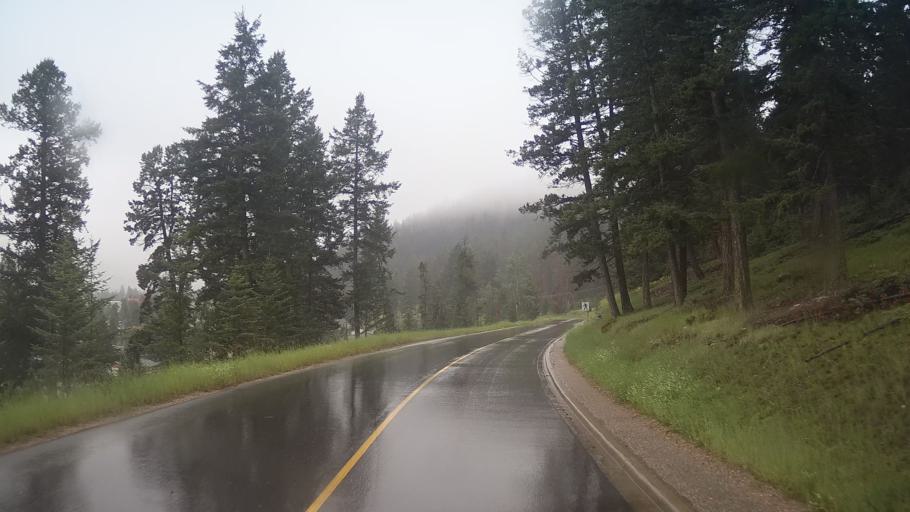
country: CA
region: Alberta
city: Jasper Park Lodge
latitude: 52.8858
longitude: -118.0836
